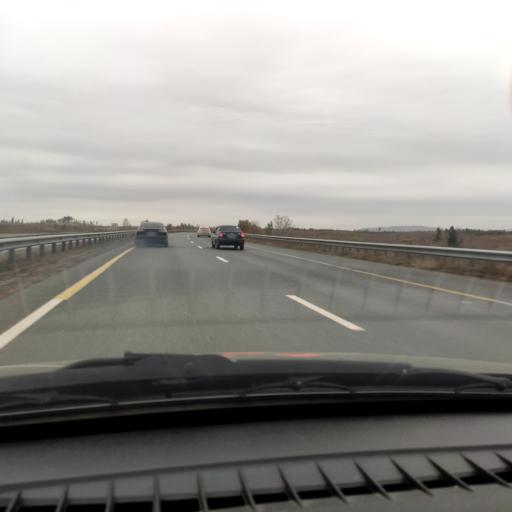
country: RU
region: Samara
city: Zhigulevsk
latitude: 53.5153
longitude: 49.5369
